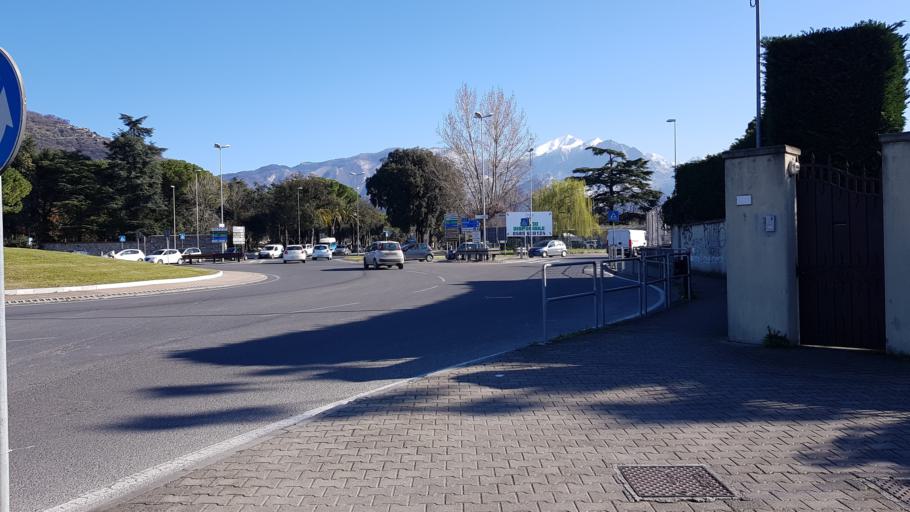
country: IT
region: Tuscany
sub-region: Provincia di Massa-Carrara
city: Carrara
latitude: 44.0547
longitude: 10.0629
